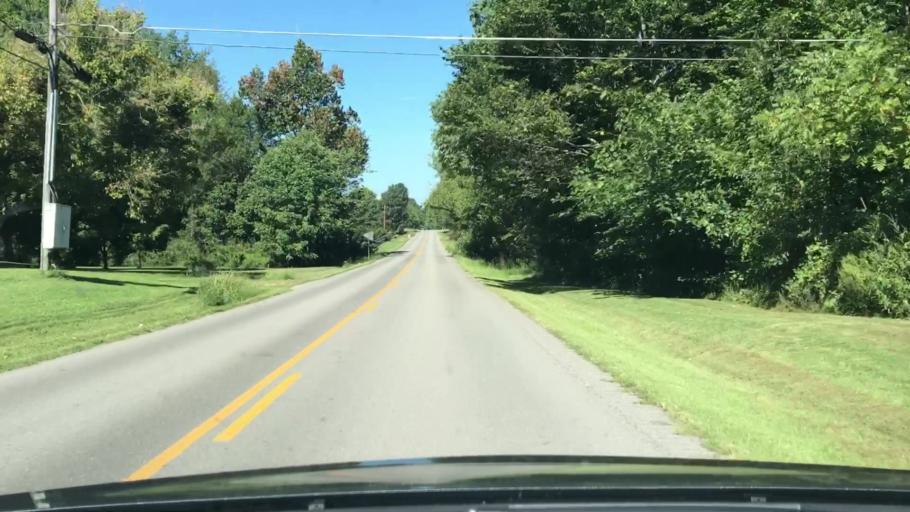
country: US
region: Kentucky
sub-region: Hardin County
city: Elizabethtown
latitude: 37.5991
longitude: -85.8775
